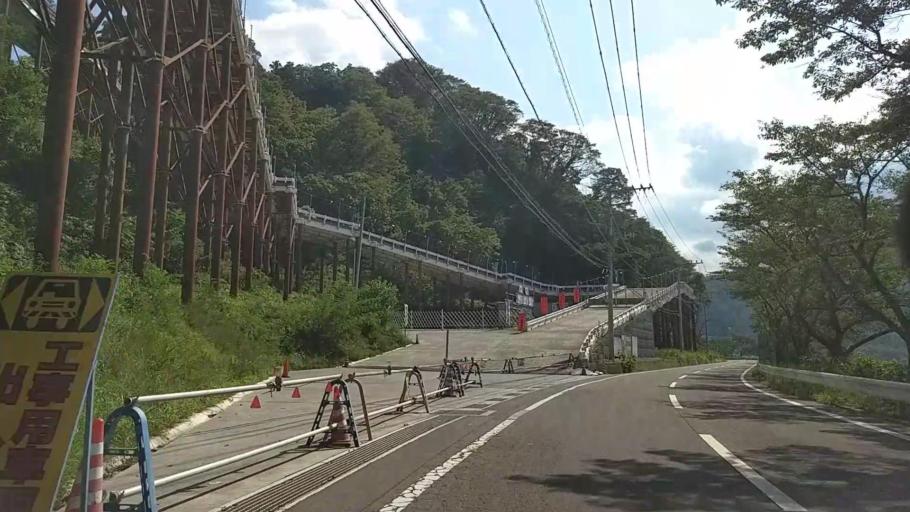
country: JP
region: Shizuoka
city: Fujinomiya
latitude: 35.3994
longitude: 138.4512
